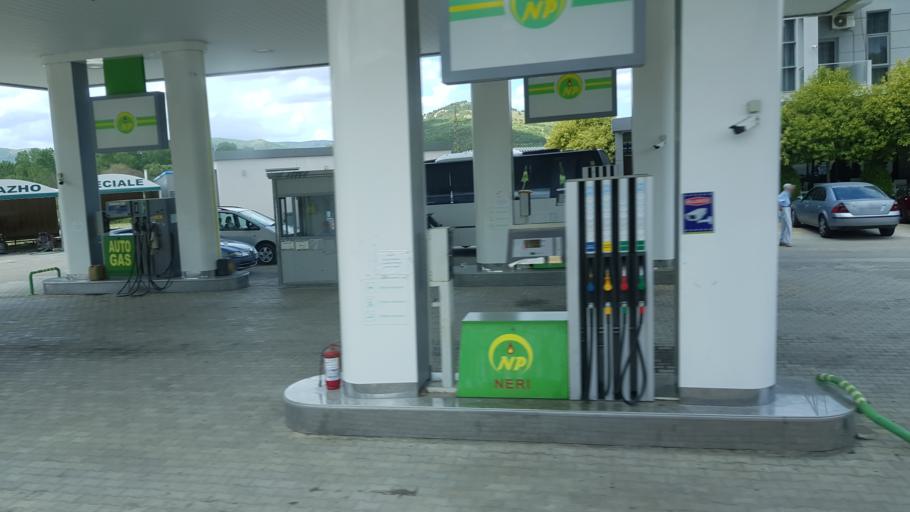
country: AL
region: Fier
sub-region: Rrethi i Mallakastres
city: Hekal
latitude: 40.5181
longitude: 19.7415
